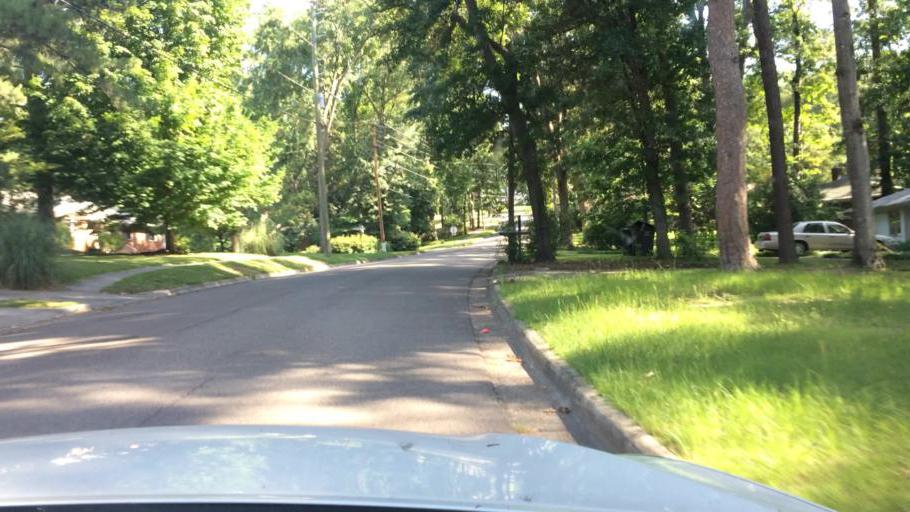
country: US
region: South Carolina
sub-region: Aiken County
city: North Augusta
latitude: 33.5059
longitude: -81.9814
